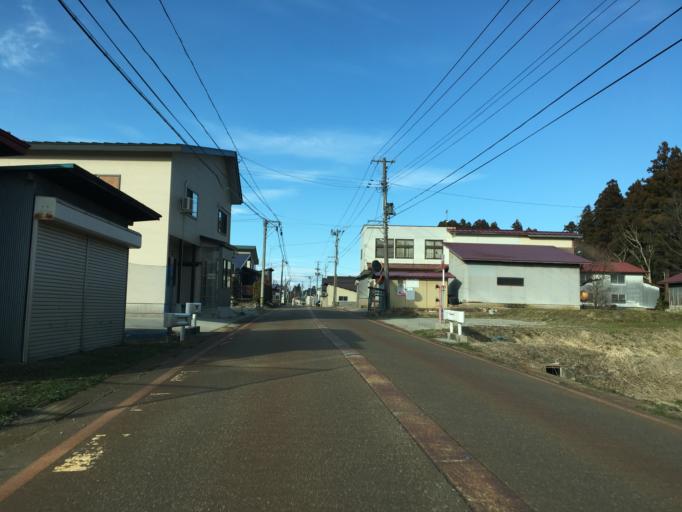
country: JP
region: Yamagata
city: Nagai
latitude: 38.0252
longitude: 139.9776
